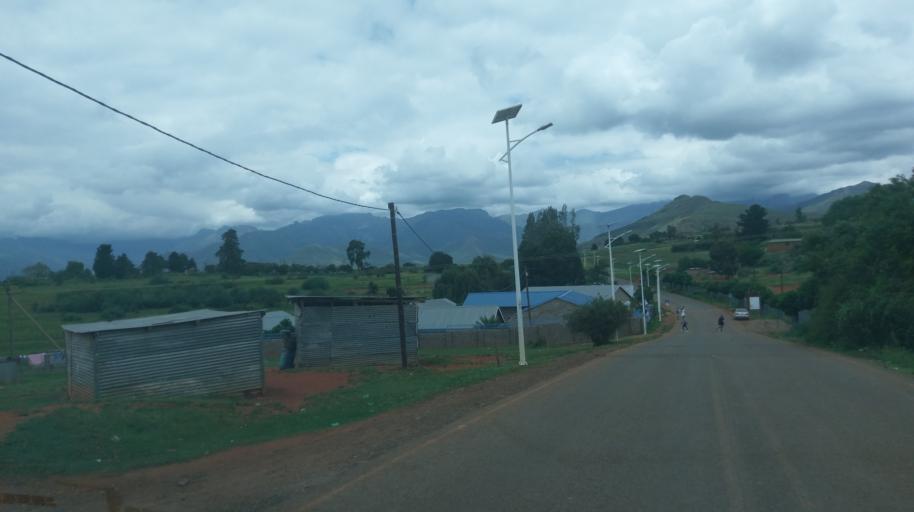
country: LS
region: Leribe
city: Leribe
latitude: -29.0094
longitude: 28.2149
